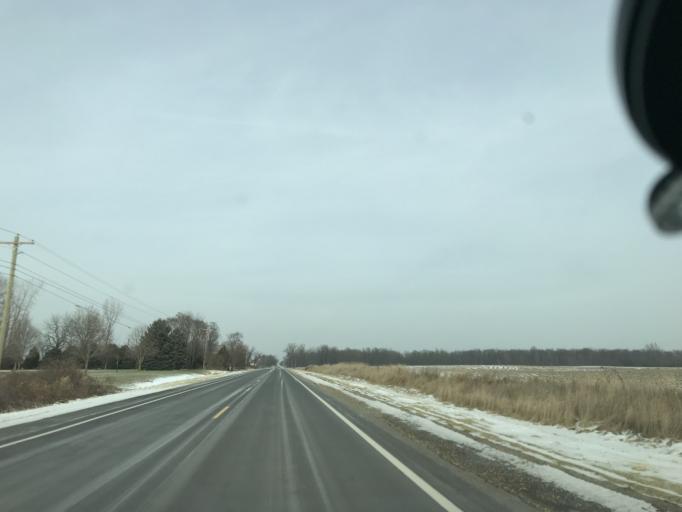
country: US
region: Michigan
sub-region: Ionia County
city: Lake Odessa
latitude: 42.8459
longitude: -85.0749
